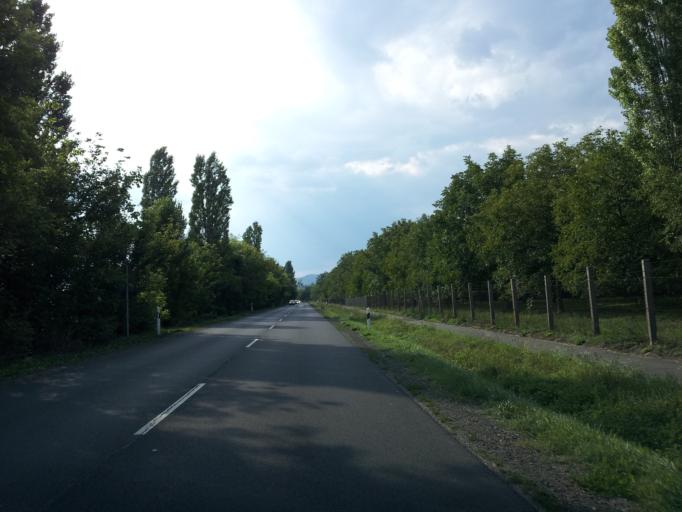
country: HU
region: Pest
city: Veroce
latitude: 47.8188
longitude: 19.0508
